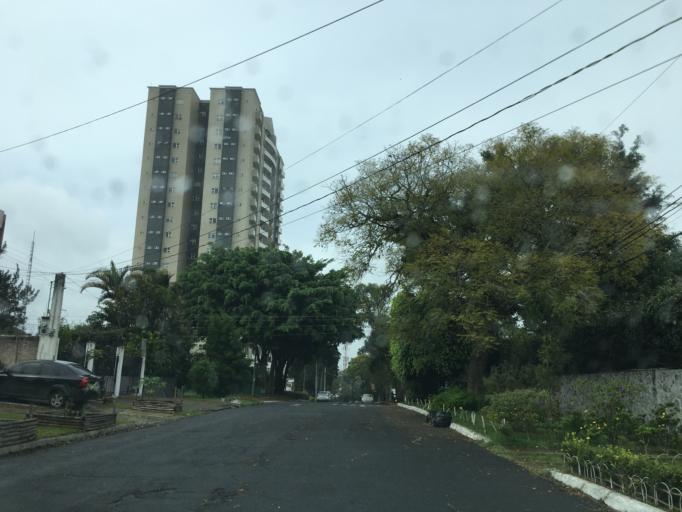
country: GT
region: Guatemala
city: Santa Catarina Pinula
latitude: 14.5869
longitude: -90.4939
